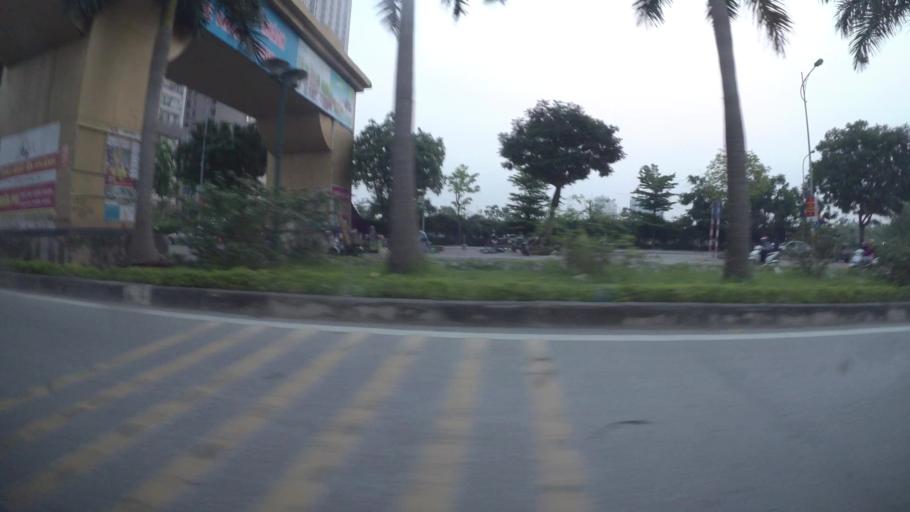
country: VN
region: Ha Noi
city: Cau Dien
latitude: 21.0095
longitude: 105.7308
